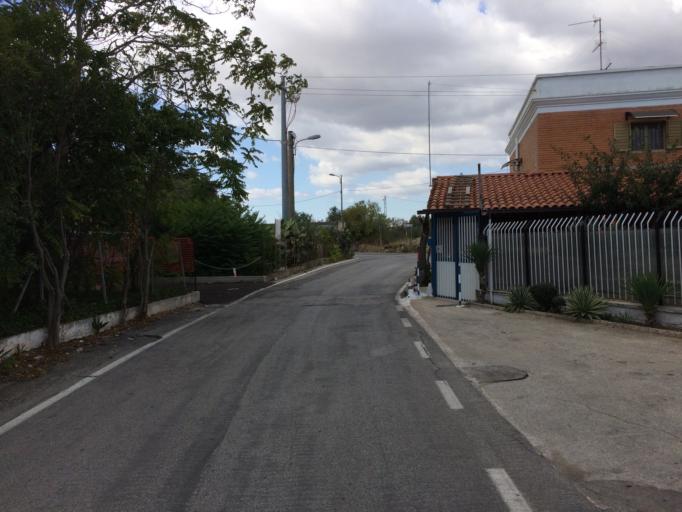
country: IT
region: Apulia
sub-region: Provincia di Bari
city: Bari
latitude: 41.1063
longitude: 16.8402
